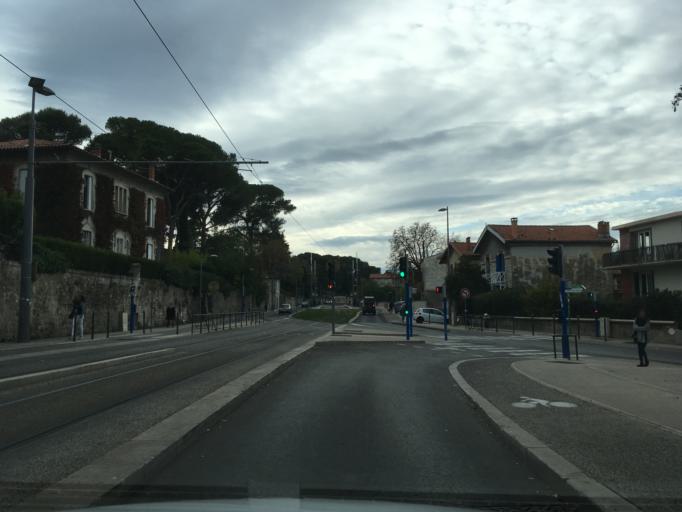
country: FR
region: Languedoc-Roussillon
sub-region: Departement de l'Herault
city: Montpellier
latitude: 43.6105
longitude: 3.8569
